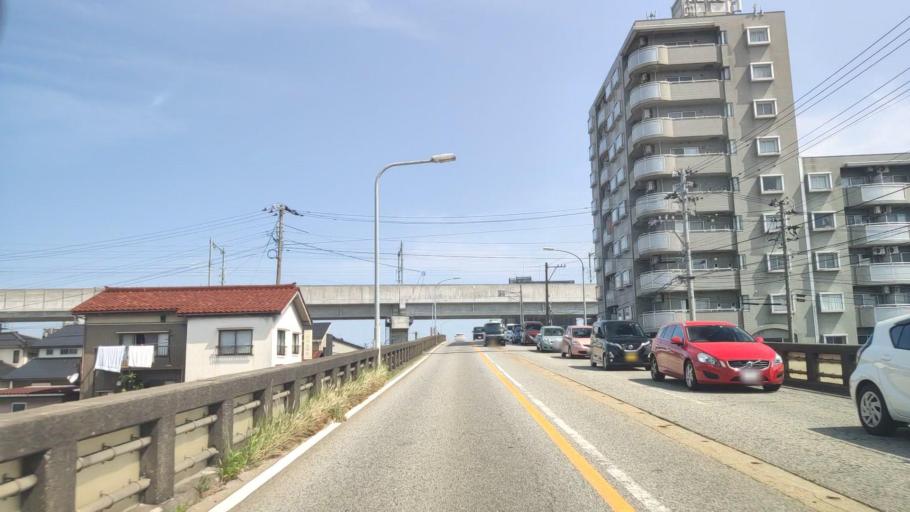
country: JP
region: Toyama
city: Toyama-shi
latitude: 36.6974
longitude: 137.2260
